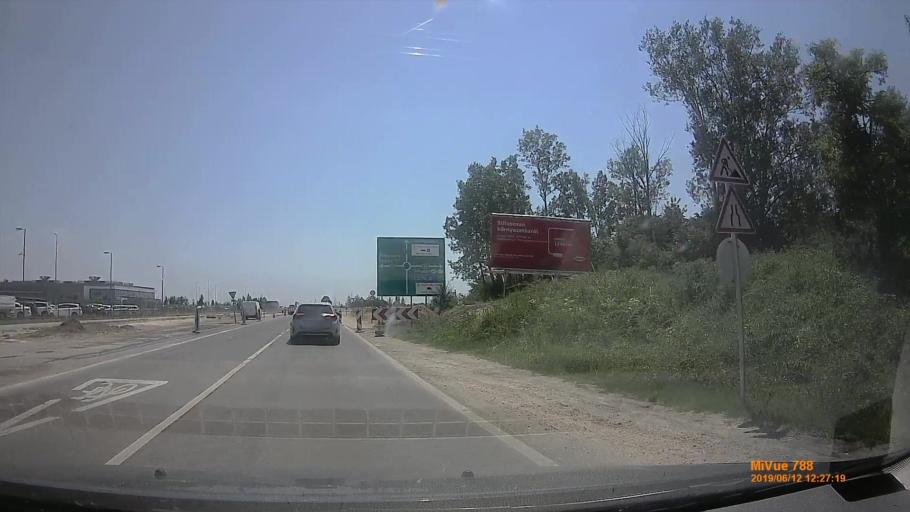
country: HU
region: Bacs-Kiskun
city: Kecskemet
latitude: 46.8810
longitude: 19.7083
